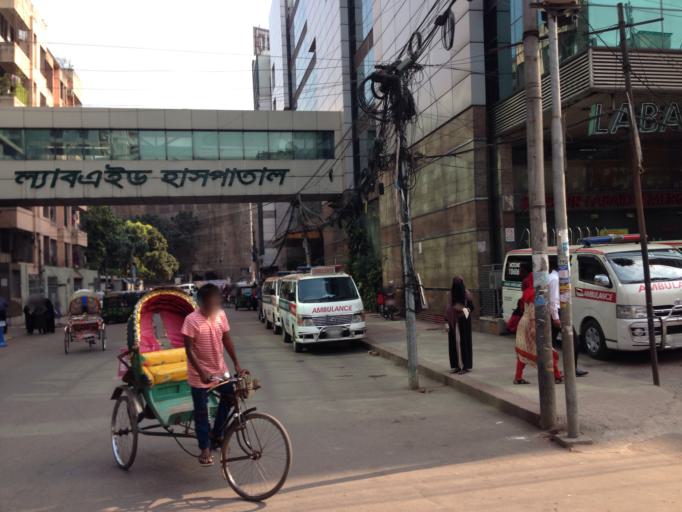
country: BD
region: Dhaka
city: Azimpur
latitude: 23.7418
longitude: 90.3830
